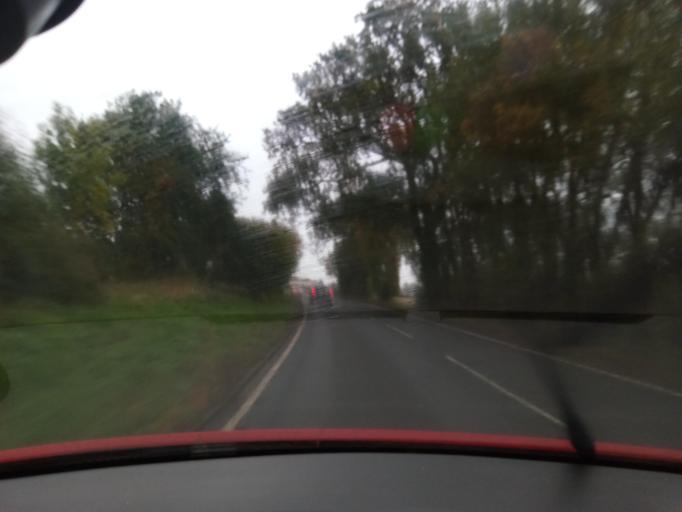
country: GB
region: England
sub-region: Suffolk
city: Kedington
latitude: 52.0548
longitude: 0.4986
